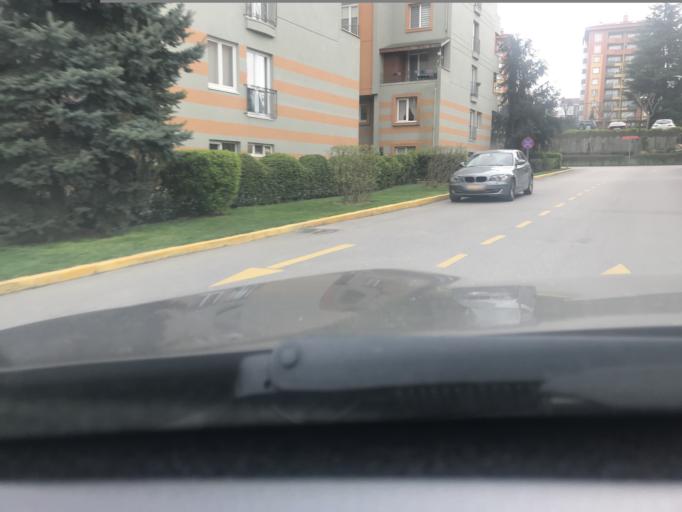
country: TR
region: Istanbul
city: Umraniye
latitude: 41.0321
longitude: 29.1573
